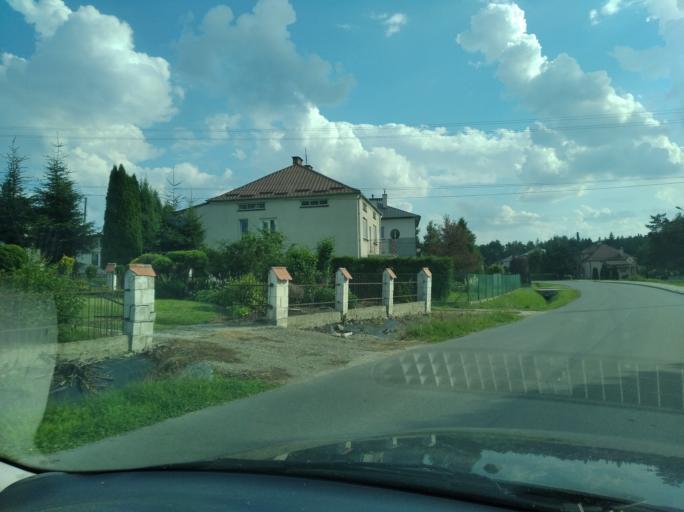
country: PL
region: Subcarpathian Voivodeship
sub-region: Powiat rzeszowski
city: Wysoka Glogowska
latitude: 50.1533
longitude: 22.0182
